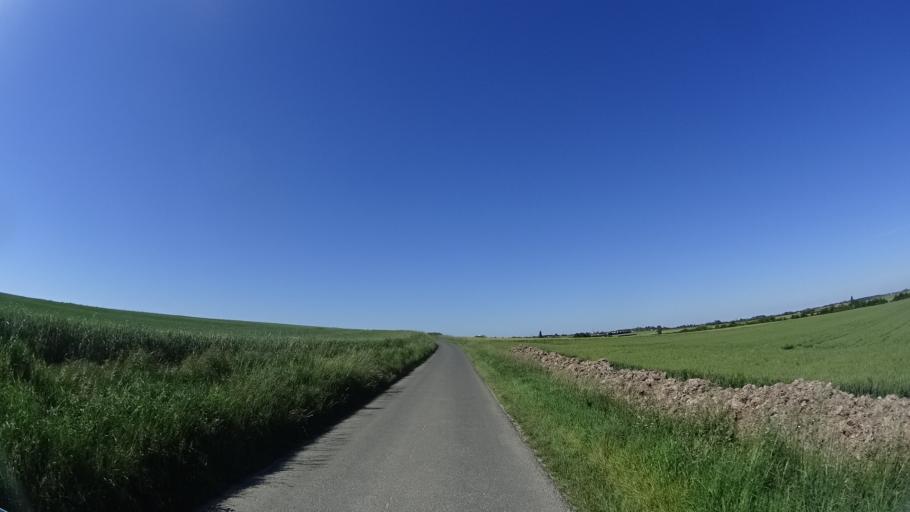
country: FR
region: Pays de la Loire
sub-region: Departement de Maine-et-Loire
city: Doue-la-Fontaine
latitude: 47.2503
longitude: -0.2873
